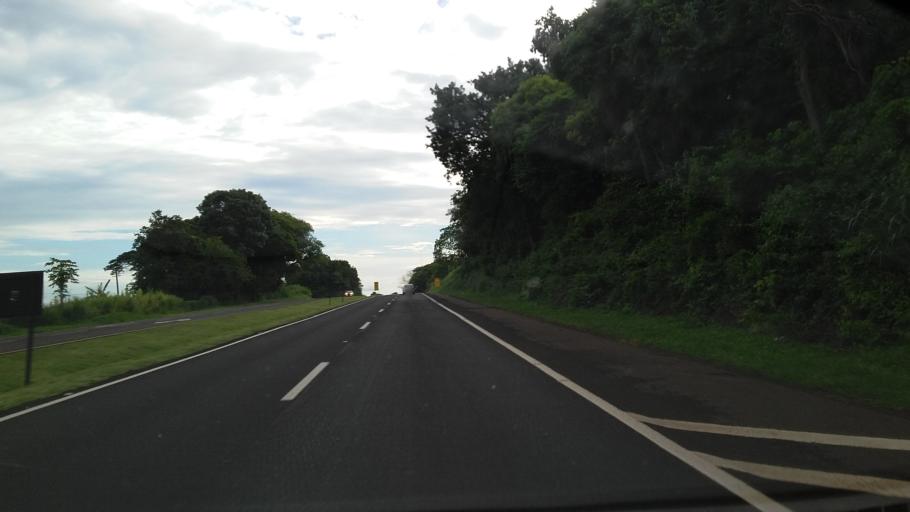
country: BR
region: Parana
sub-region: Paicandu
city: Paicandu
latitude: -23.5063
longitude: -52.0212
